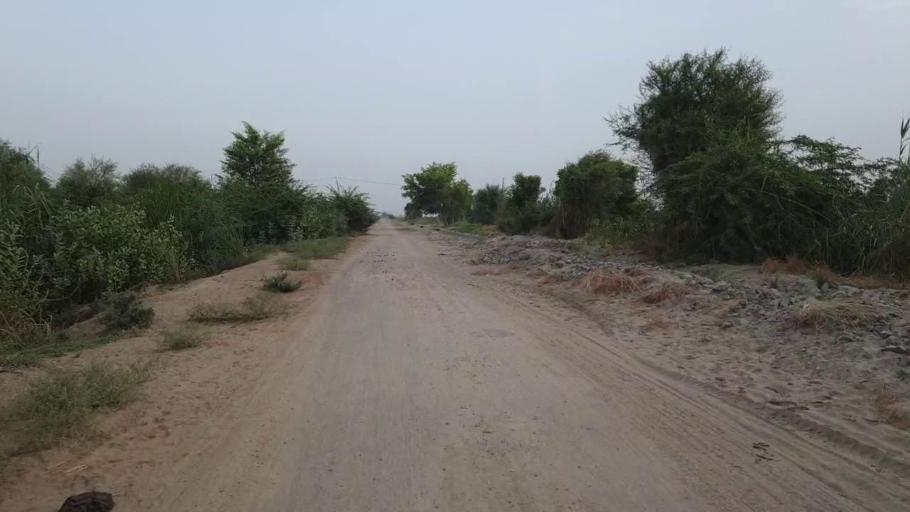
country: PK
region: Sindh
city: Daur
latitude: 26.4175
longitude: 68.2251
